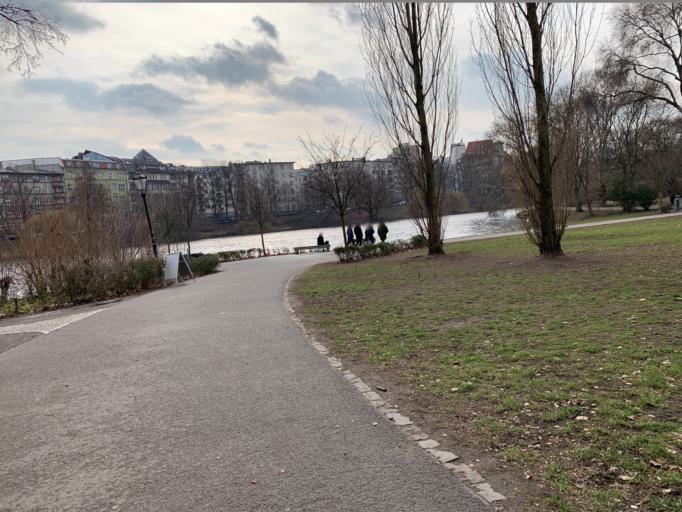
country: DE
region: Berlin
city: Charlottenburg Bezirk
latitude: 52.5095
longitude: 13.2918
